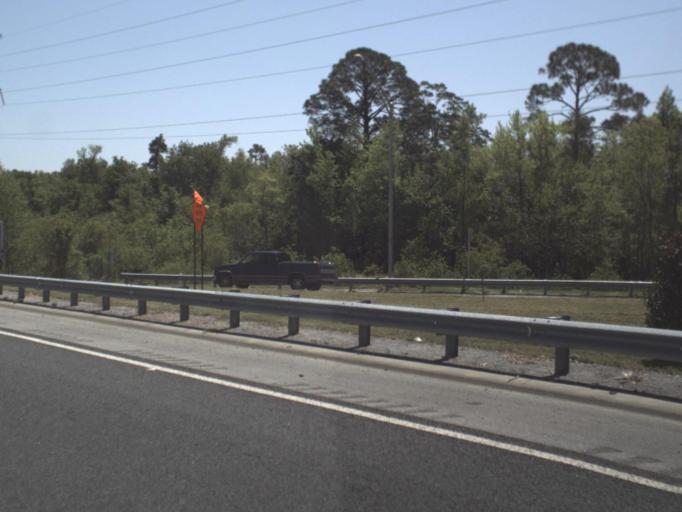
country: US
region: Florida
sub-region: Escambia County
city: Ferry Pass
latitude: 30.5034
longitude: -87.2190
